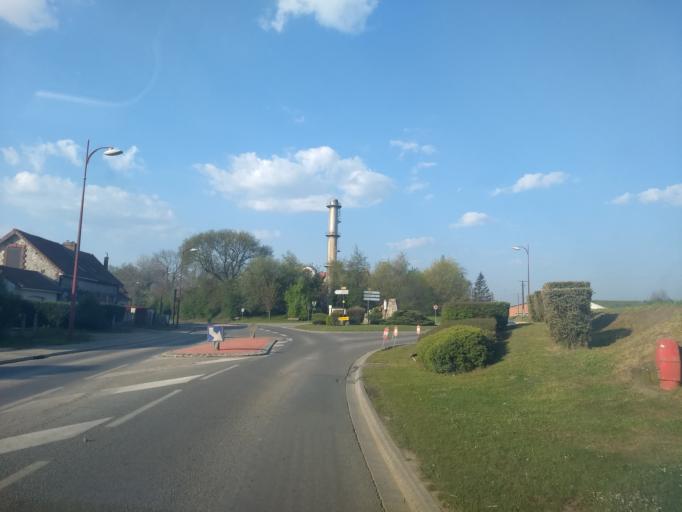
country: FR
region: Nord-Pas-de-Calais
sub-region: Departement du Pas-de-Calais
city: Agny
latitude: 50.1978
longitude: 2.7470
